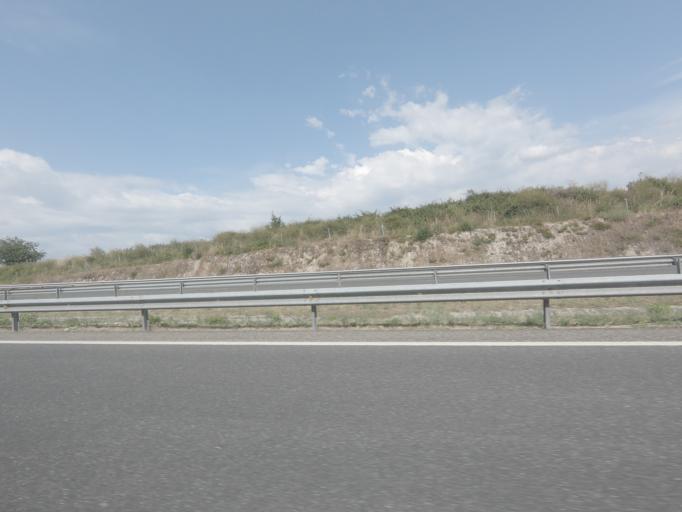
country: ES
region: Galicia
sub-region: Provincia de Ourense
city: Ourense
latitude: 42.3170
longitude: -7.8867
